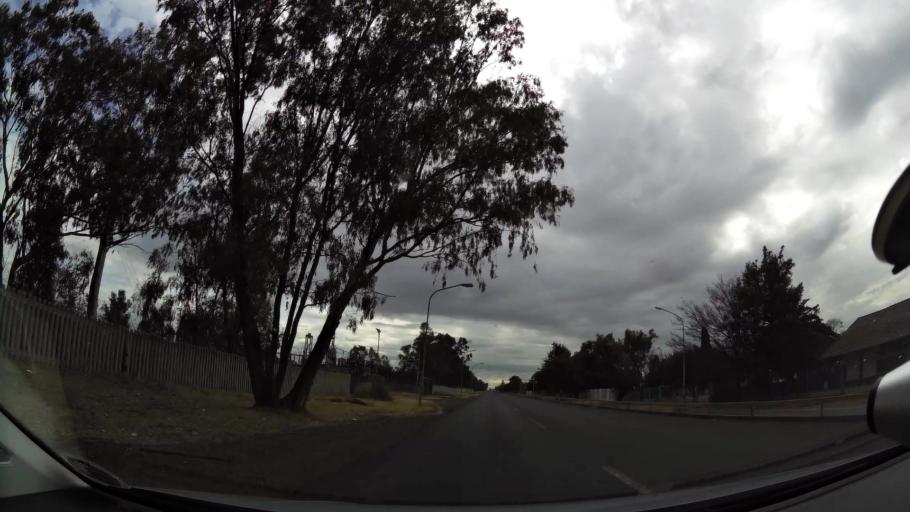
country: ZA
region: Orange Free State
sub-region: Fezile Dabi District Municipality
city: Kroonstad
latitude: -27.6398
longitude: 27.2202
